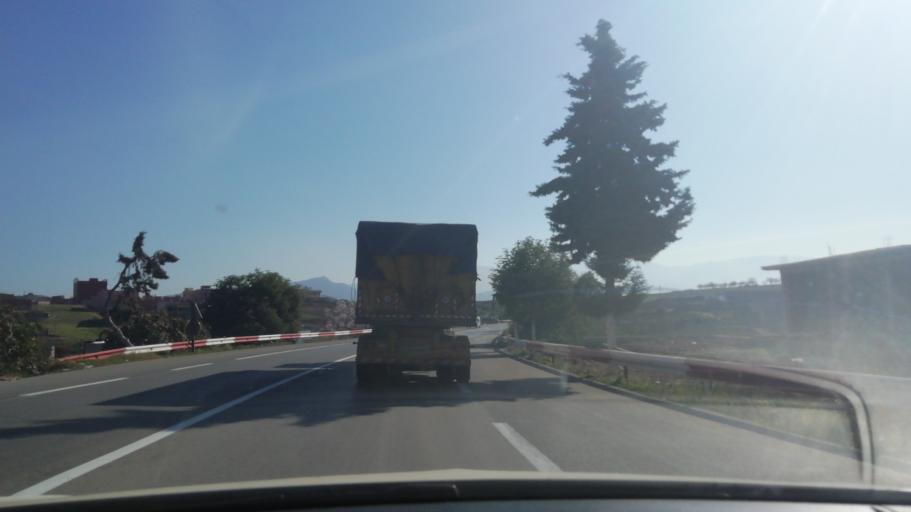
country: DZ
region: Tlemcen
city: Nedroma
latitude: 35.0749
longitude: -1.7791
